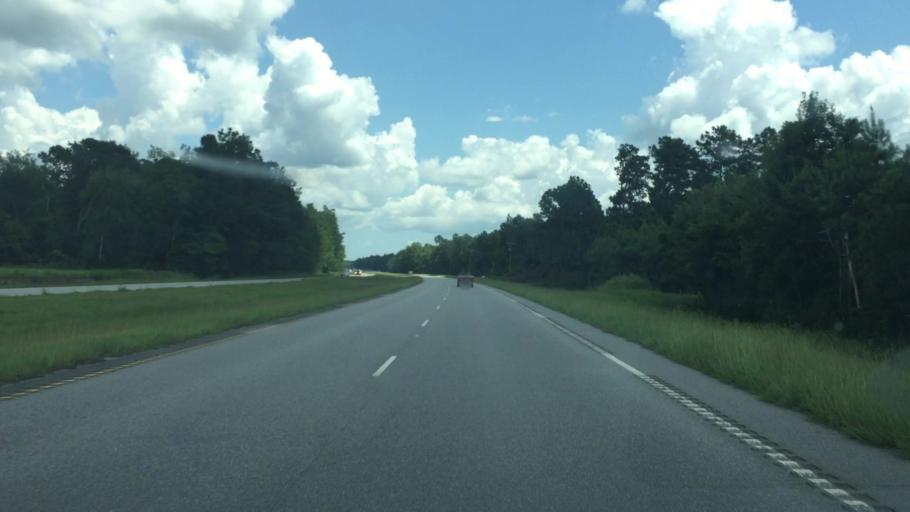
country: US
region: South Carolina
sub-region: Horry County
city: Loris
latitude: 34.0476
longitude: -78.8337
